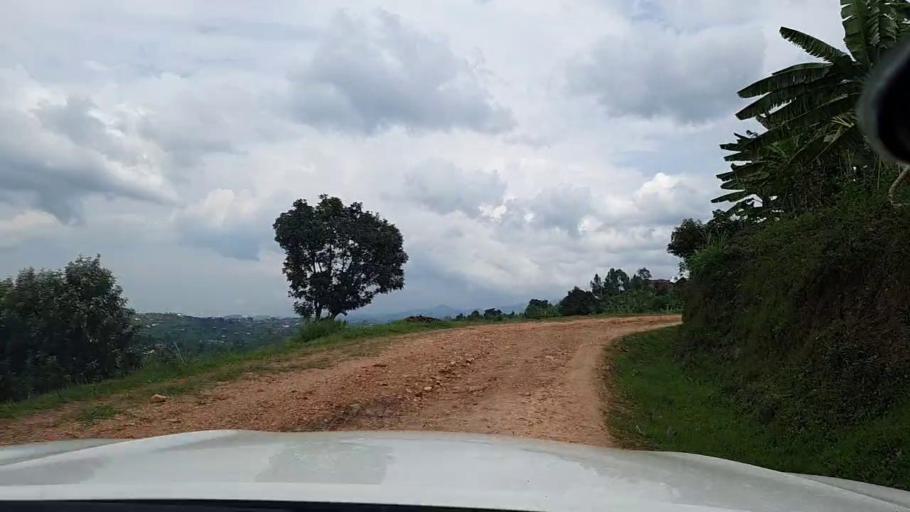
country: RW
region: Western Province
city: Kibuye
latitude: -2.0770
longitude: 29.4222
